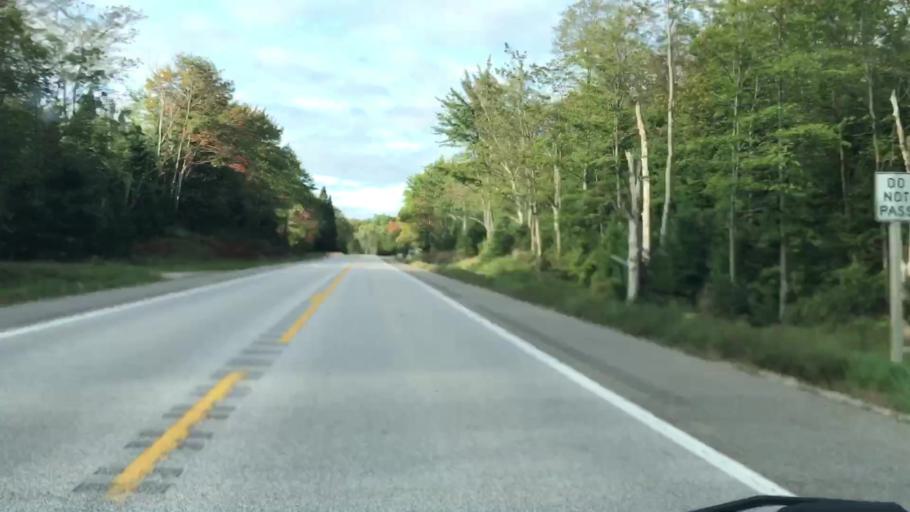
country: US
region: Michigan
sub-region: Luce County
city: Newberry
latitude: 46.3357
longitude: -85.0473
